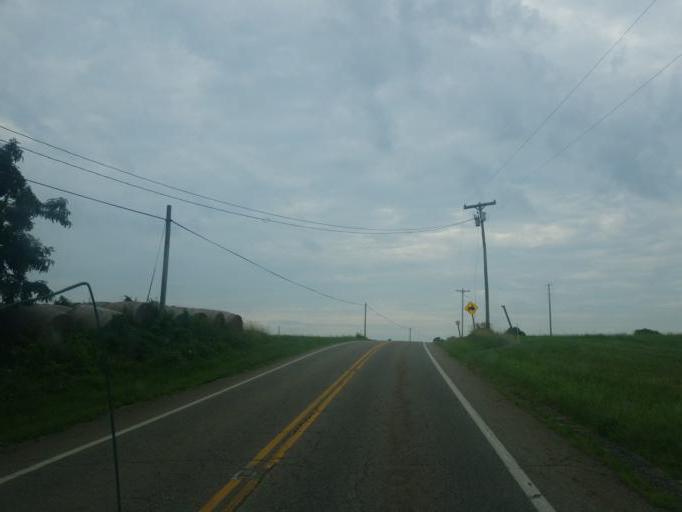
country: US
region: Ohio
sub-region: Carroll County
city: Lake Mohawk
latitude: 40.6503
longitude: -81.2363
